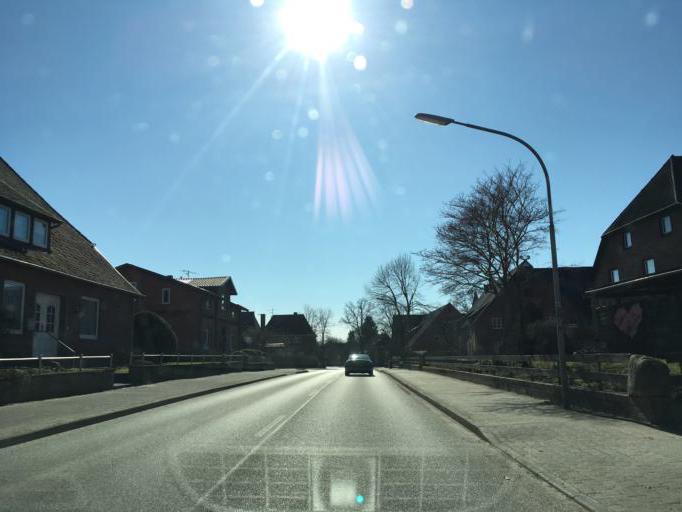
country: DE
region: Schleswig-Holstein
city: Berkenthin
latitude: 53.7325
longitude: 10.6510
